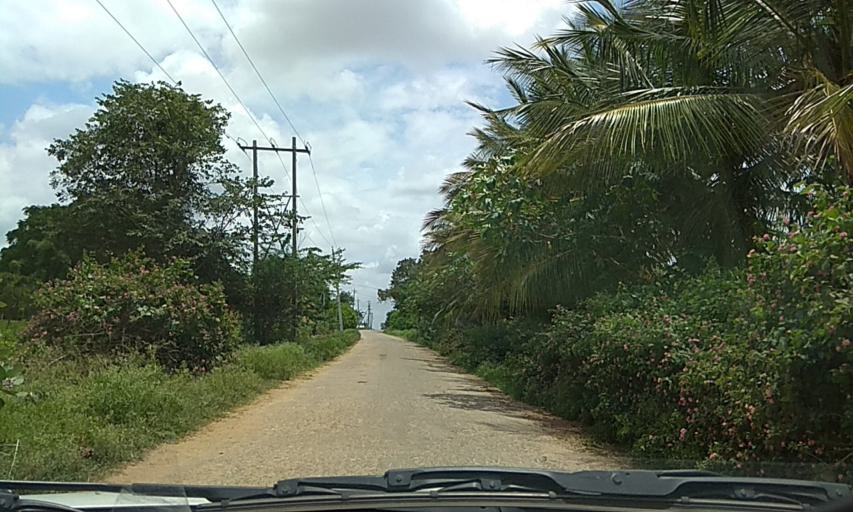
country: IN
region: Karnataka
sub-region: Chamrajnagar
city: Gundlupet
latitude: 11.8877
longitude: 76.6964
